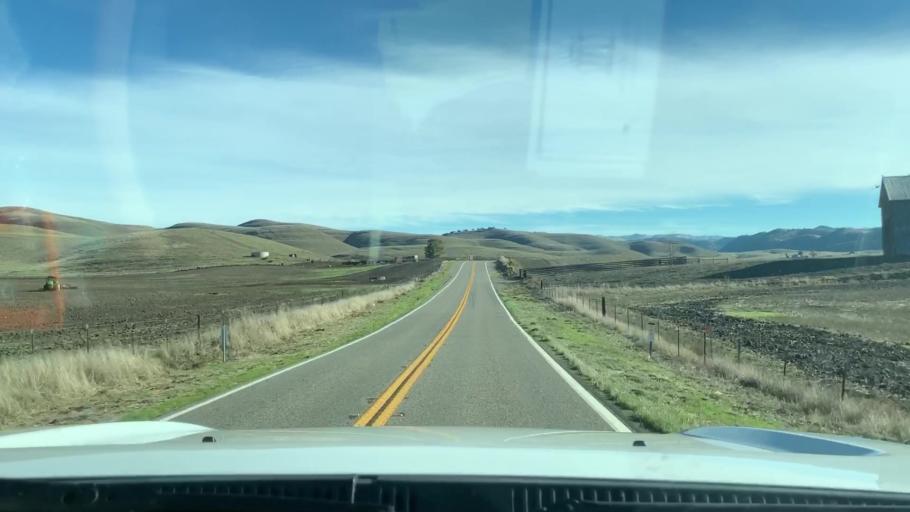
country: US
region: California
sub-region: Monterey County
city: King City
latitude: 36.1651
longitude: -120.8866
